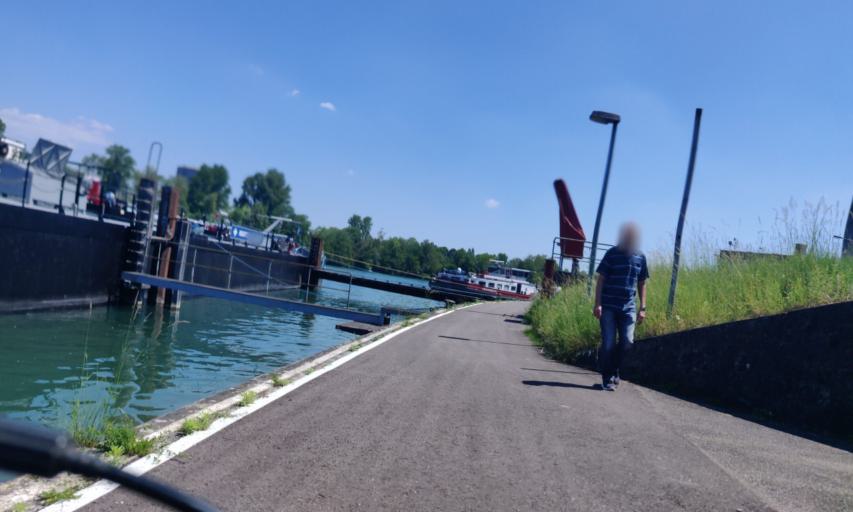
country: DE
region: Baden-Wuerttemberg
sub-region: Freiburg Region
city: Grenzach-Wyhlen
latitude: 47.5450
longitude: 7.6587
